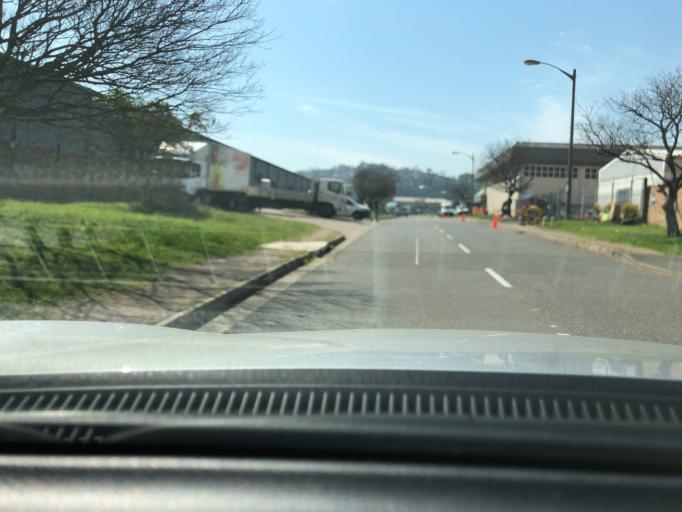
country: ZA
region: KwaZulu-Natal
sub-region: eThekwini Metropolitan Municipality
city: Berea
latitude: -29.8062
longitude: 30.9965
